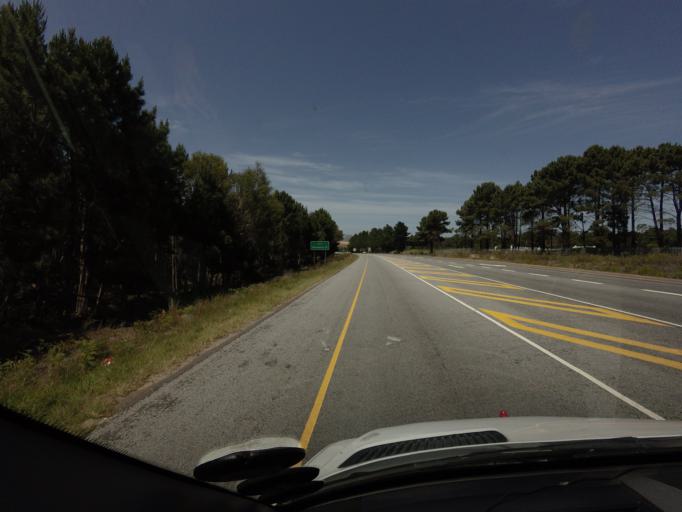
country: ZA
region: Western Cape
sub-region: Overberg District Municipality
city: Hermanus
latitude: -34.2990
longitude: 19.1434
